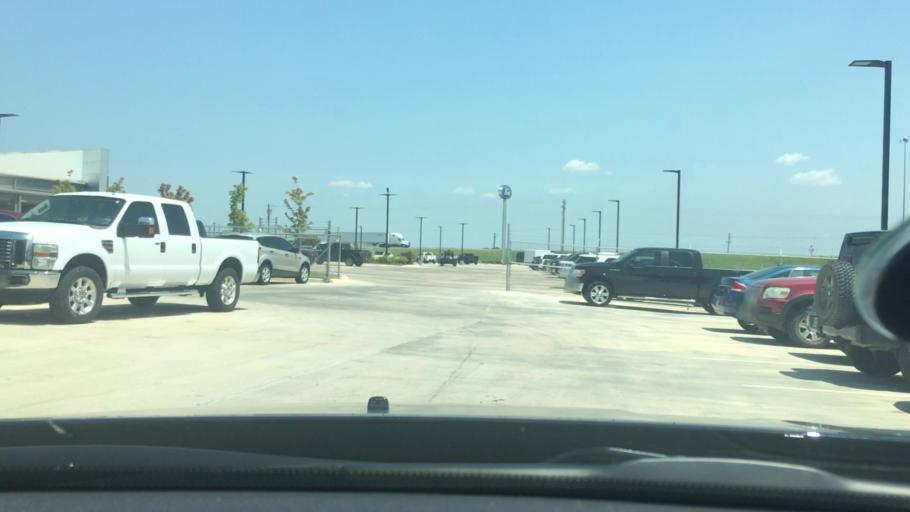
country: US
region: Oklahoma
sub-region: Garvin County
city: Pauls Valley
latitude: 34.7416
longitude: -97.2685
